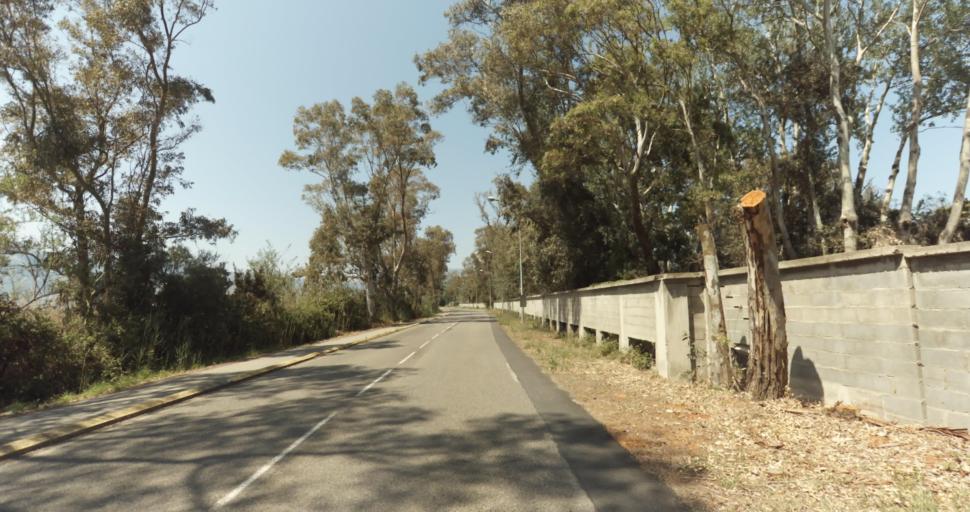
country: FR
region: Corsica
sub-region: Departement de la Haute-Corse
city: Biguglia
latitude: 42.6125
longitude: 9.4811
